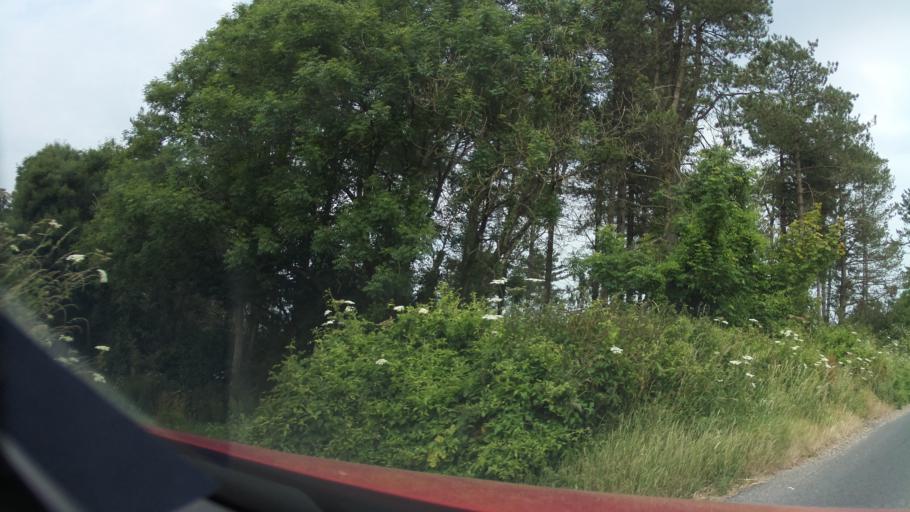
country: GB
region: England
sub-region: Devon
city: Colyton
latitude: 50.7126
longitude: -3.1322
